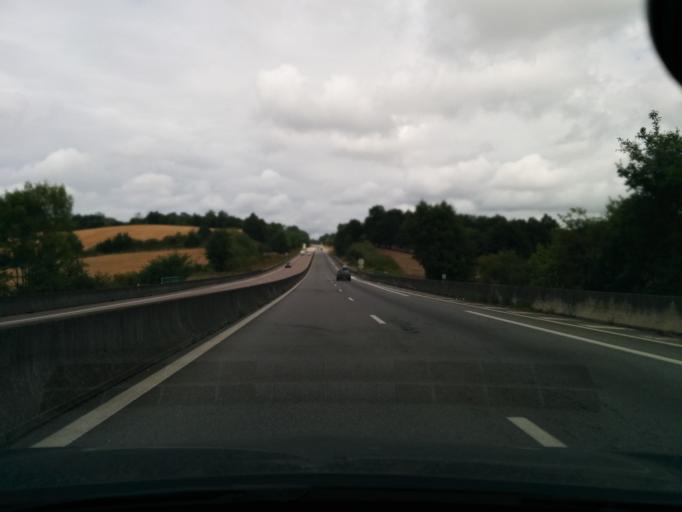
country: FR
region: Limousin
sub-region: Departement de la Haute-Vienne
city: Boisseuil
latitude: 45.7324
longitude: 1.3404
